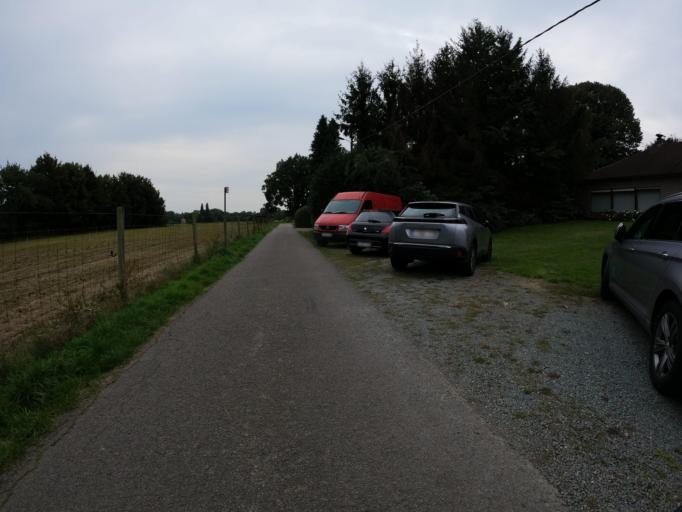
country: BE
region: Flanders
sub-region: Provincie Antwerpen
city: Wommelgem
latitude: 51.2080
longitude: 4.5343
